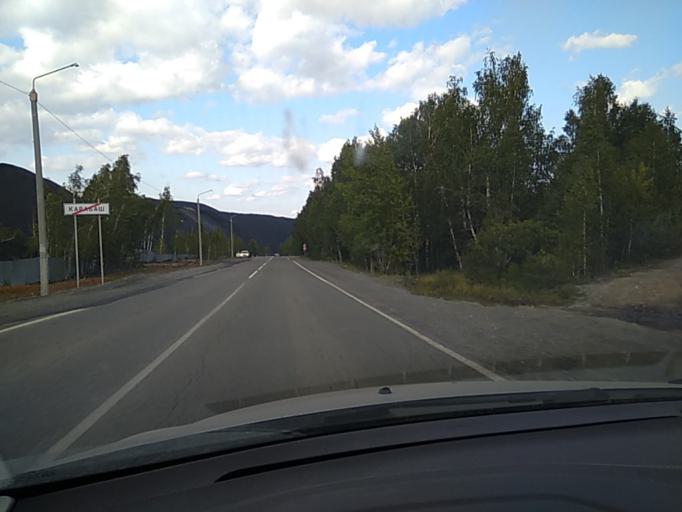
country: RU
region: Chelyabinsk
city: Karabash
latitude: 55.4928
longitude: 60.2444
